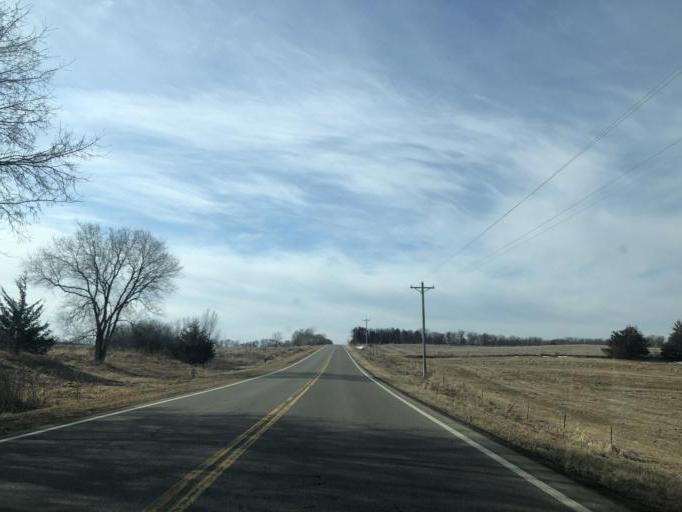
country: US
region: Minnesota
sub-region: Sherburne County
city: Becker
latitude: 45.4221
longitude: -93.8502
